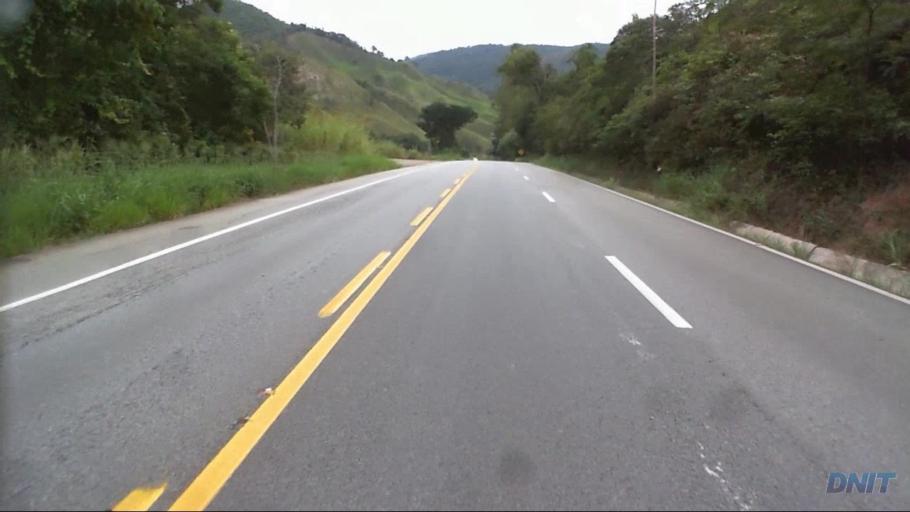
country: BR
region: Minas Gerais
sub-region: Nova Era
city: Nova Era
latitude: -19.6252
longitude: -42.8660
